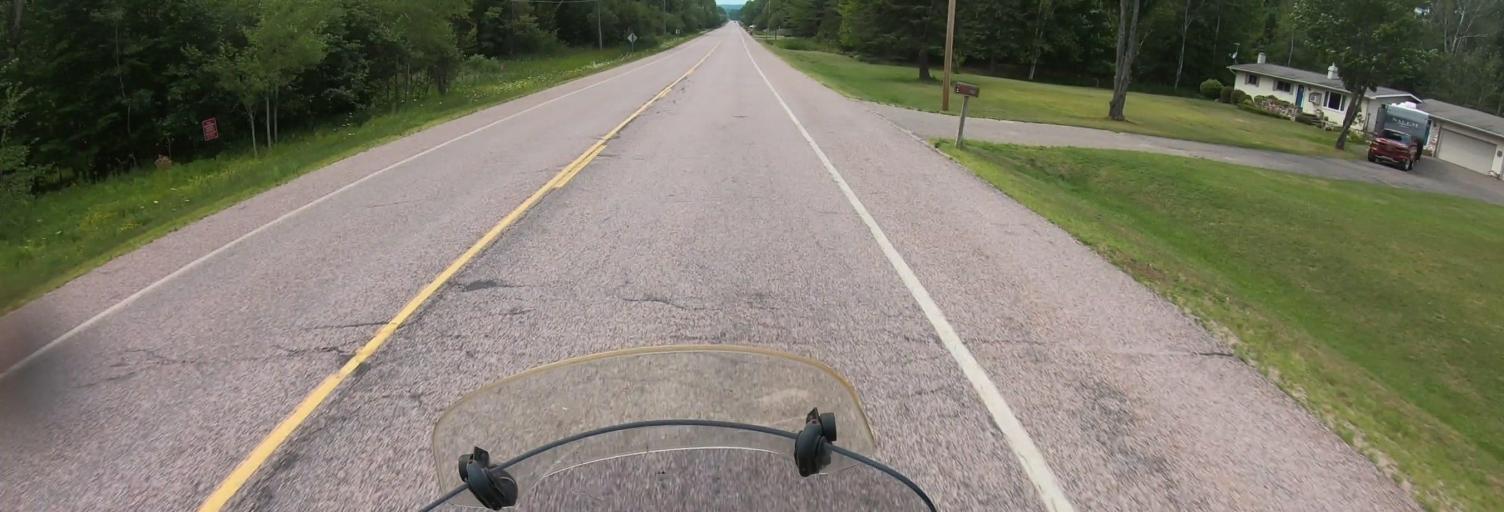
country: US
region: Michigan
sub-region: Marquette County
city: Harvey
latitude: 46.4633
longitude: -87.3267
